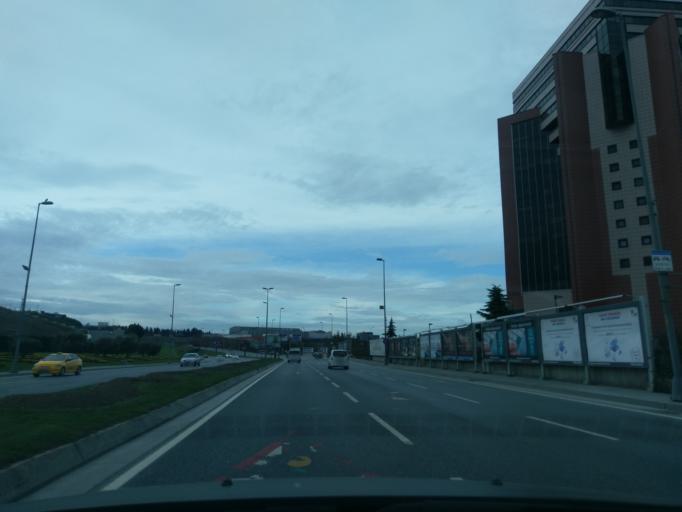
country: TR
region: Istanbul
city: Bahcelievler
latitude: 40.9844
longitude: 28.8317
